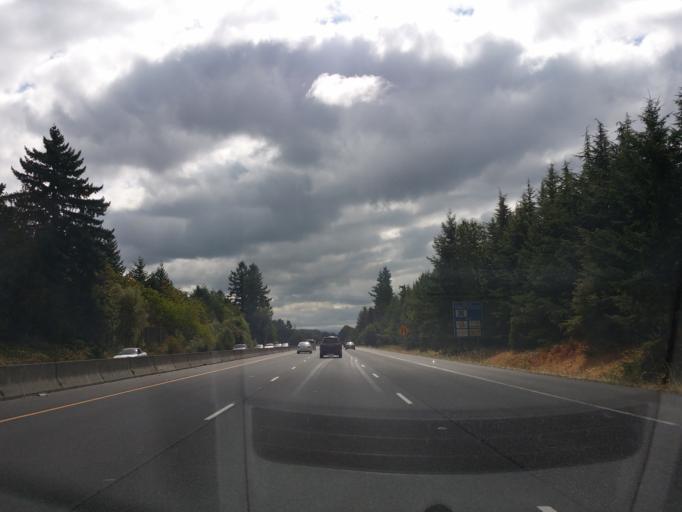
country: US
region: Washington
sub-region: Clark County
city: Mill Plain
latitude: 45.5993
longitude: -122.5335
